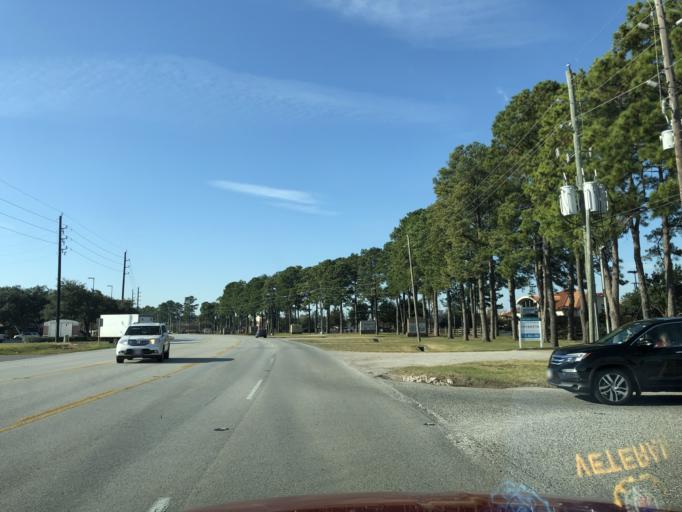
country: US
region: Texas
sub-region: Harris County
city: Tomball
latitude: 30.0358
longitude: -95.5530
